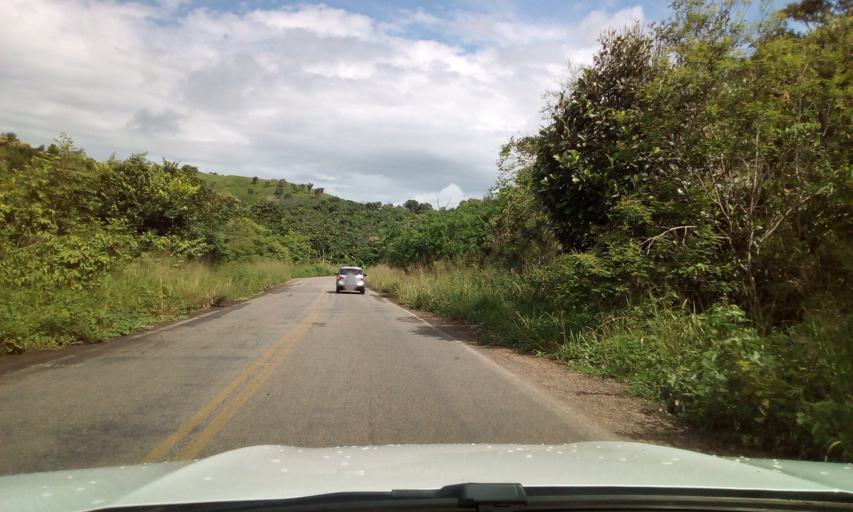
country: BR
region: Paraiba
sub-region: Areia
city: Areia
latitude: -6.9298
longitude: -35.6492
